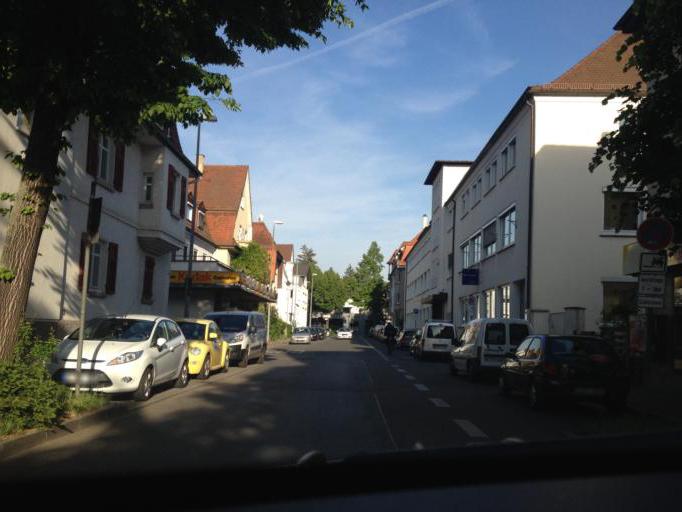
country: DE
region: Baden-Wuerttemberg
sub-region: Regierungsbezirk Stuttgart
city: Esslingen
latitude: 48.7407
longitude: 9.3159
